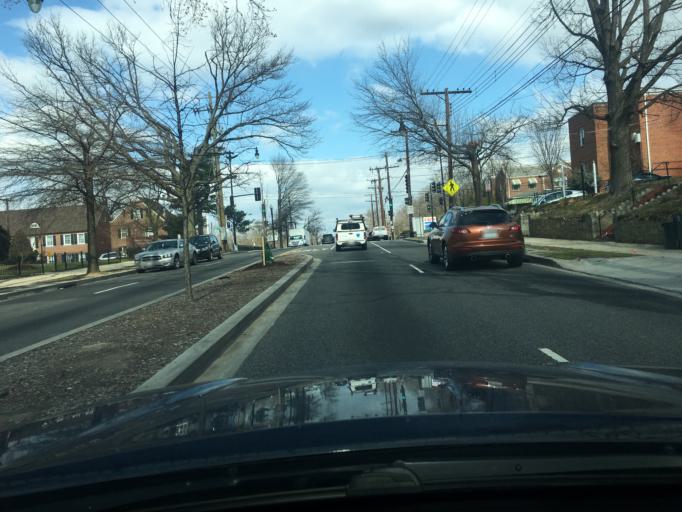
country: US
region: Maryland
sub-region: Prince George's County
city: Silver Hill
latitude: 38.8647
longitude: -76.9491
